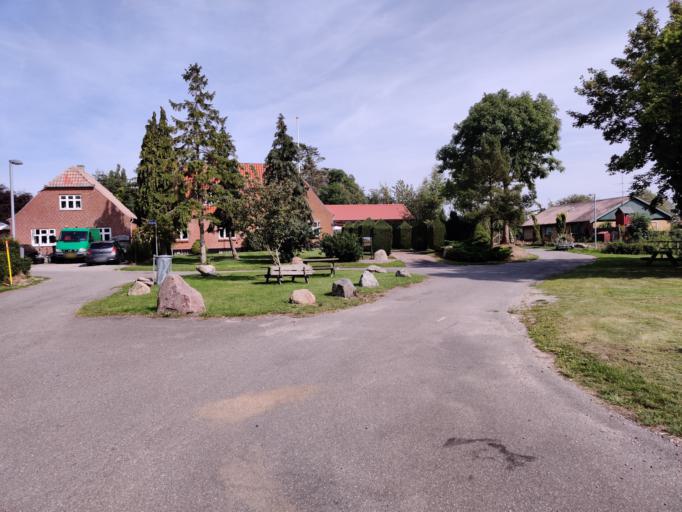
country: DK
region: Zealand
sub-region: Guldborgsund Kommune
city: Nykobing Falster
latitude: 54.6331
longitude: 11.9044
